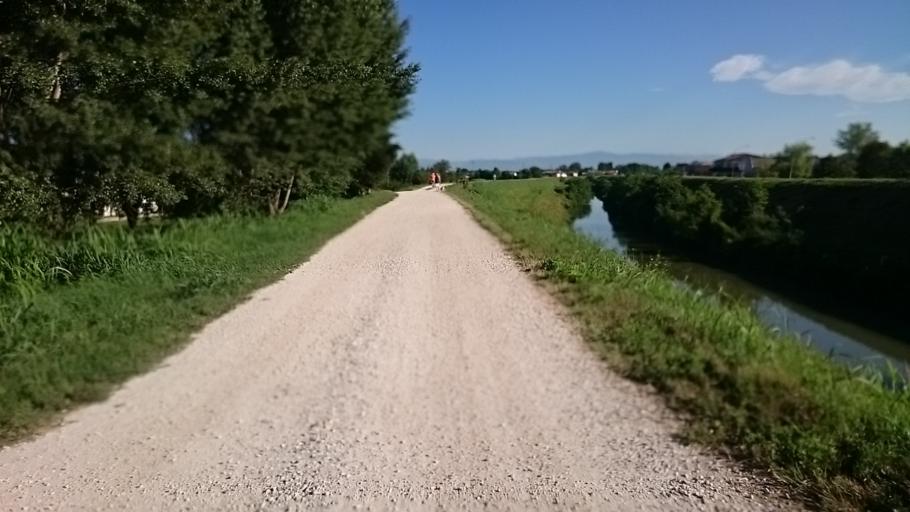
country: IT
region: Veneto
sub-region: Provincia di Padova
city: Vigodarzere
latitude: 45.4603
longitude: 11.8947
